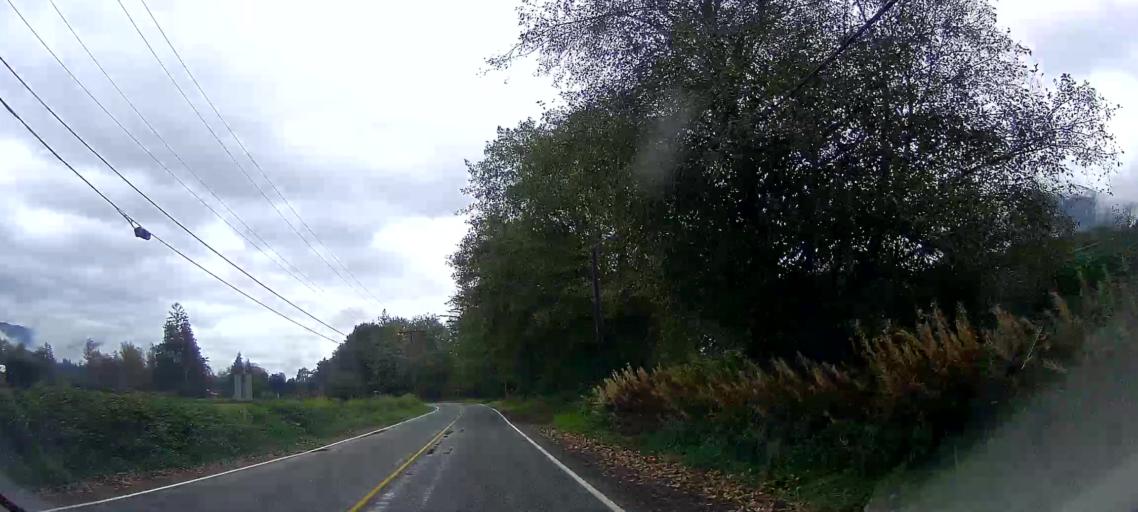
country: US
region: Washington
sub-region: Skagit County
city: Sedro-Woolley
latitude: 48.5269
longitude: -122.0296
